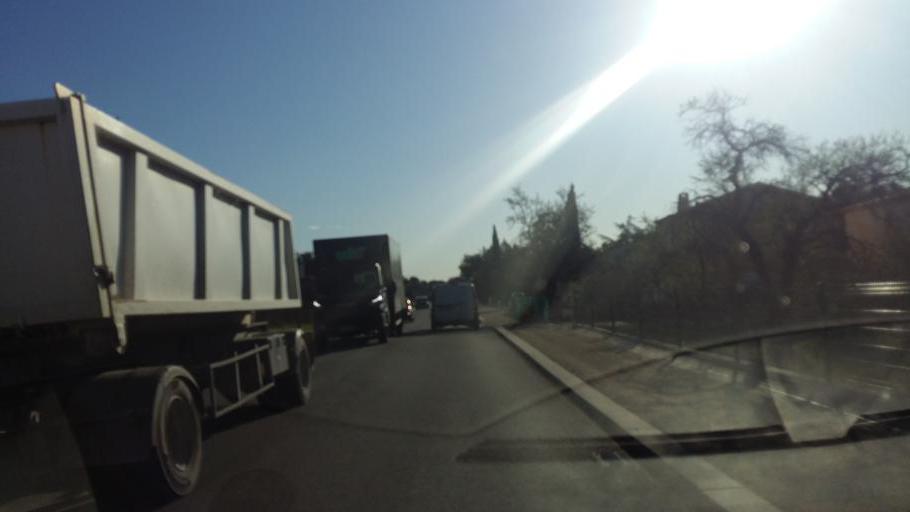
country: FR
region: Provence-Alpes-Cote d'Azur
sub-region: Departement du Vaucluse
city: Merindol
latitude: 43.7510
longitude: 5.2077
